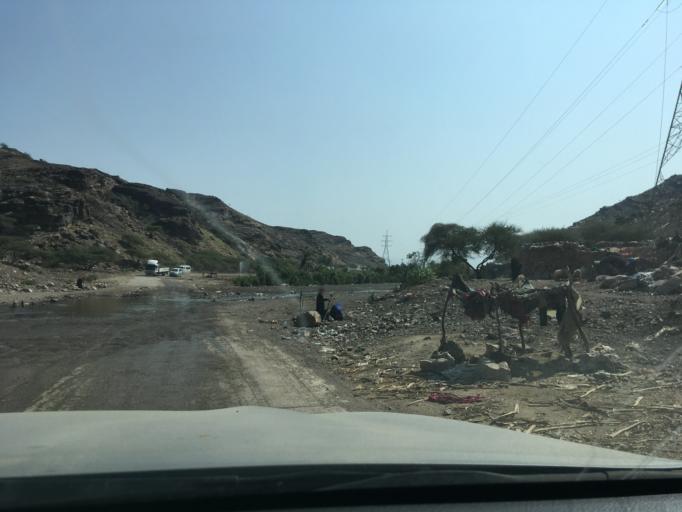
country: YE
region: Lahij
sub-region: Al Milah
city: Al Milah
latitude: 13.3575
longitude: 44.7698
